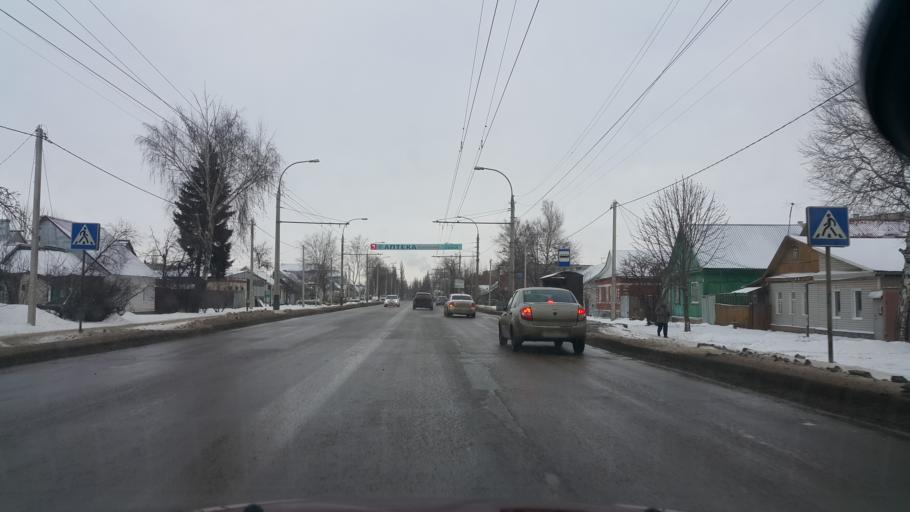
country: RU
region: Tambov
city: Tambov
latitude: 52.7296
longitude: 41.4025
